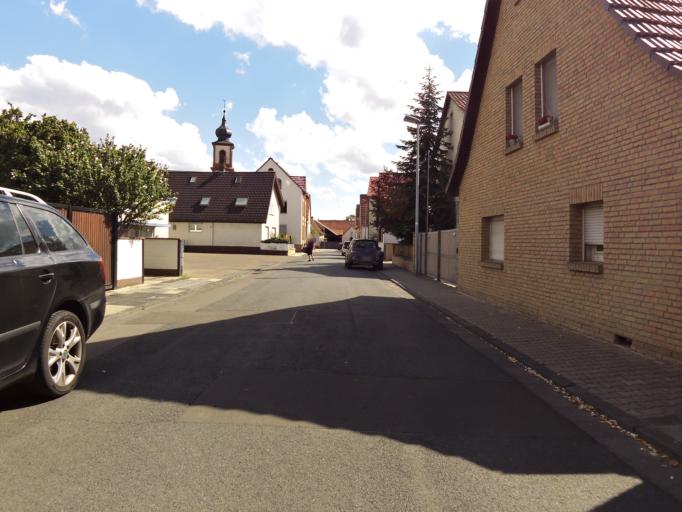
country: DE
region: Hesse
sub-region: Regierungsbezirk Darmstadt
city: Burstadt
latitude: 49.6574
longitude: 8.4131
